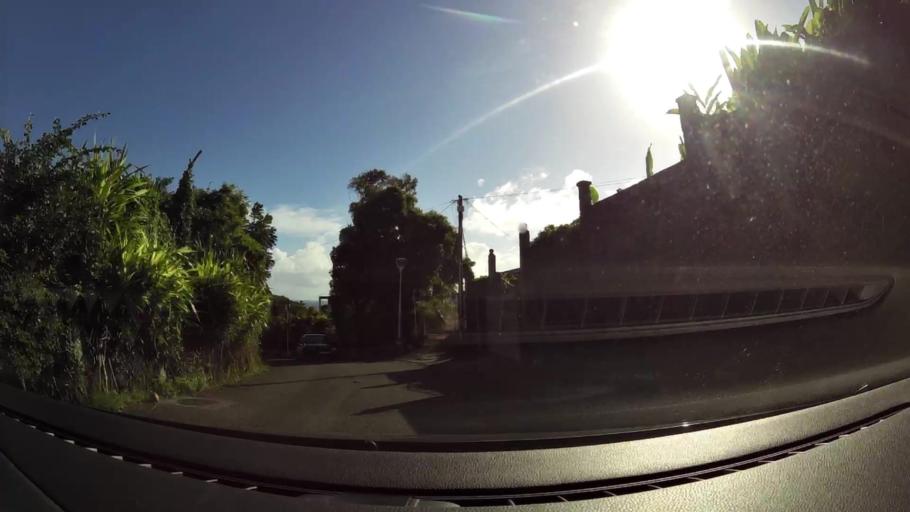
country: GP
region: Guadeloupe
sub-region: Guadeloupe
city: Le Gosier
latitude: 16.2032
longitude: -61.4748
